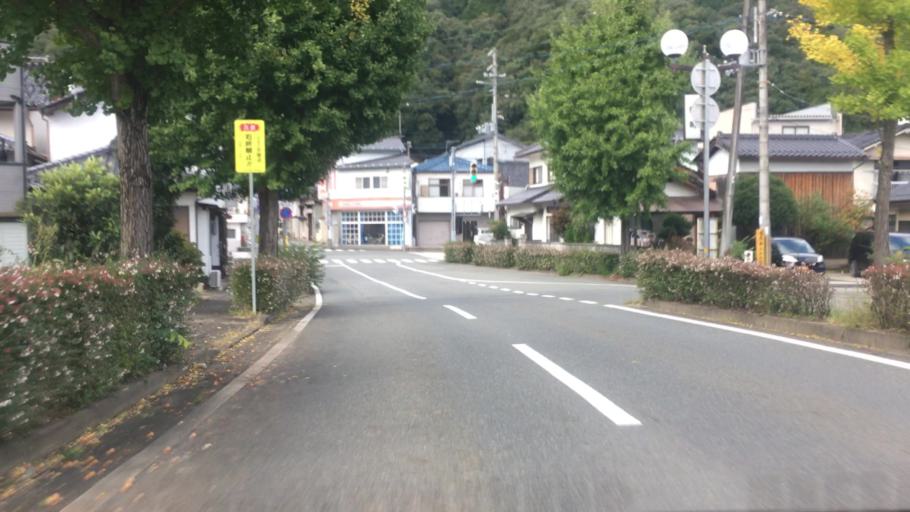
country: JP
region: Hyogo
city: Toyooka
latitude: 35.4051
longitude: 134.7646
